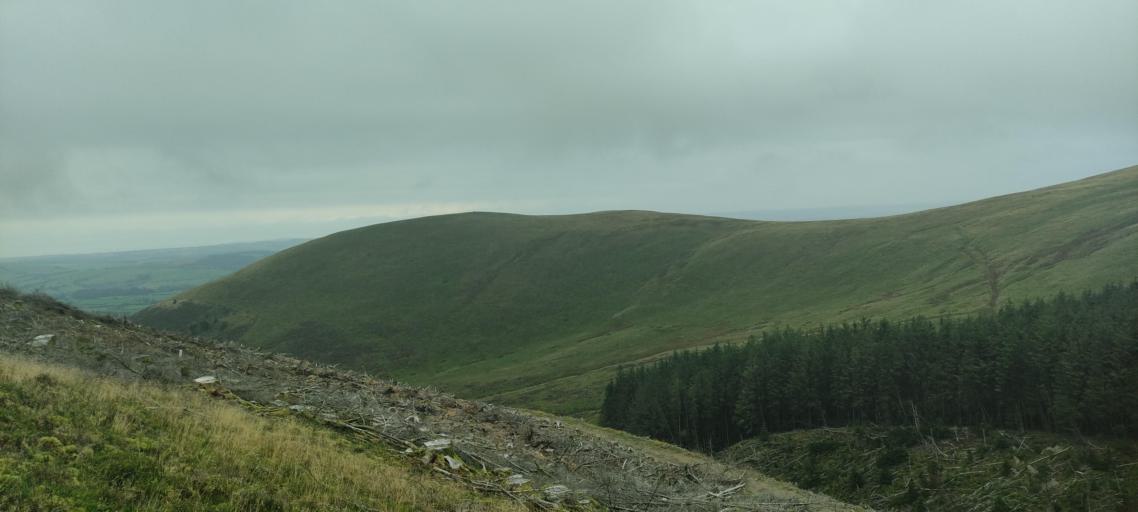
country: GB
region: England
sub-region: Cumbria
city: Cockermouth
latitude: 54.5696
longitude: -3.3827
